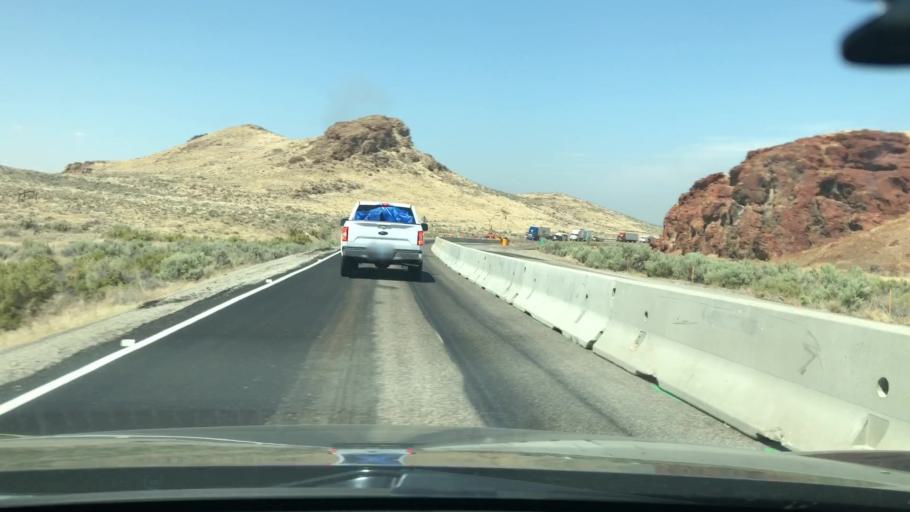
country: US
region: Idaho
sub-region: Owyhee County
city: Marsing
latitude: 43.4592
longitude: -116.8656
